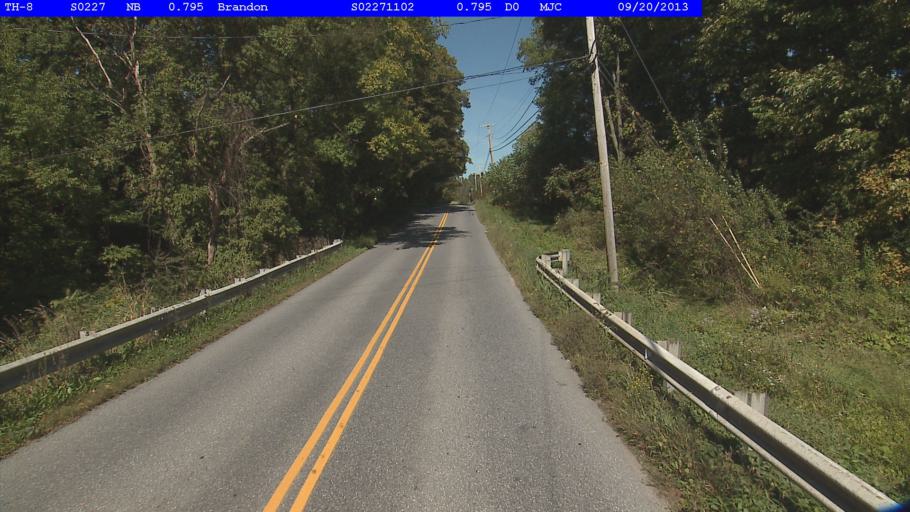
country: US
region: Vermont
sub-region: Rutland County
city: Brandon
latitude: 43.7858
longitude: -73.0535
